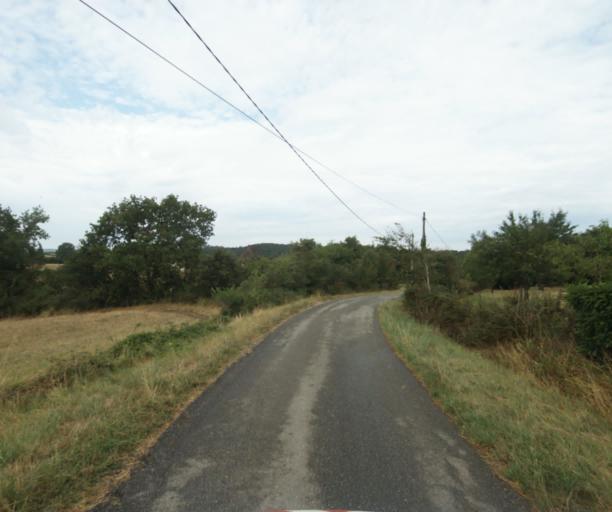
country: FR
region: Midi-Pyrenees
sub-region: Departement de la Haute-Garonne
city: Revel
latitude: 43.4272
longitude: 1.9960
